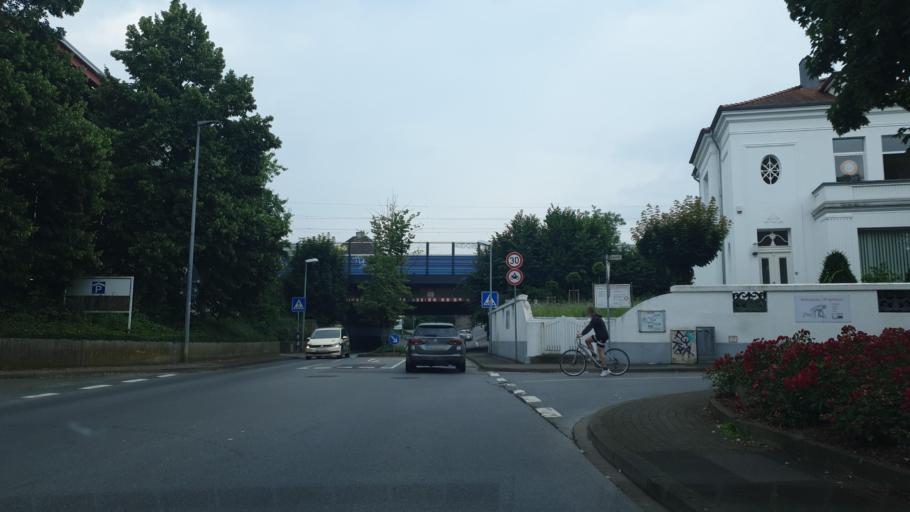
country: DE
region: North Rhine-Westphalia
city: Bad Oeynhausen
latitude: 52.2053
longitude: 8.7913
